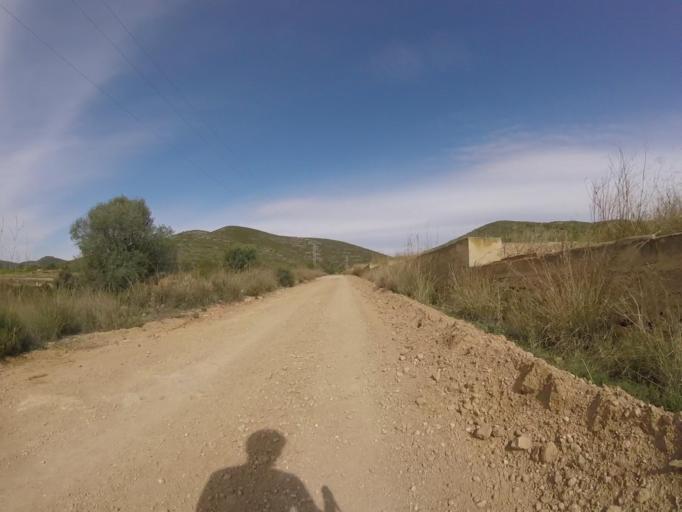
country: ES
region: Valencia
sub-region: Provincia de Castello
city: Torreblanca
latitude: 40.1963
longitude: 0.1589
